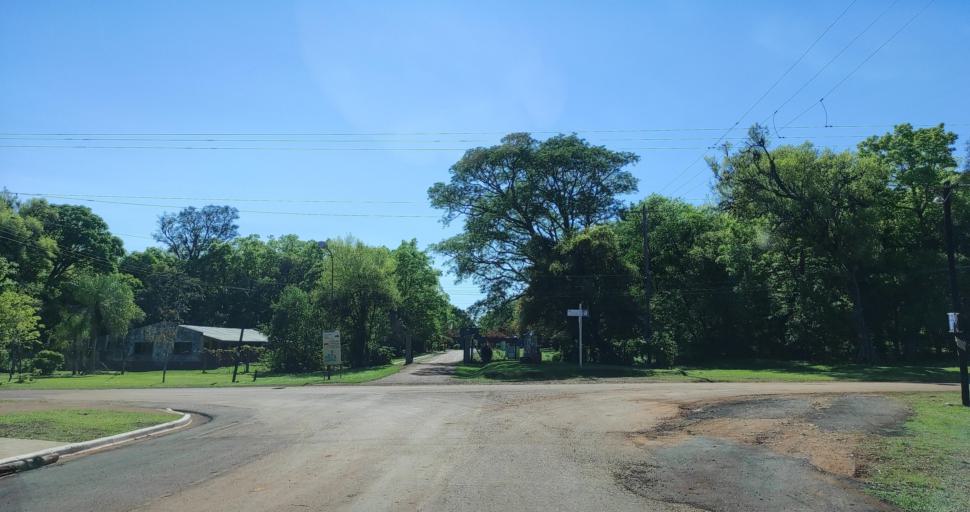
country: AR
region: Misiones
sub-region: Departamento de Candelaria
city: Loreto
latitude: -27.3334
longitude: -55.5217
